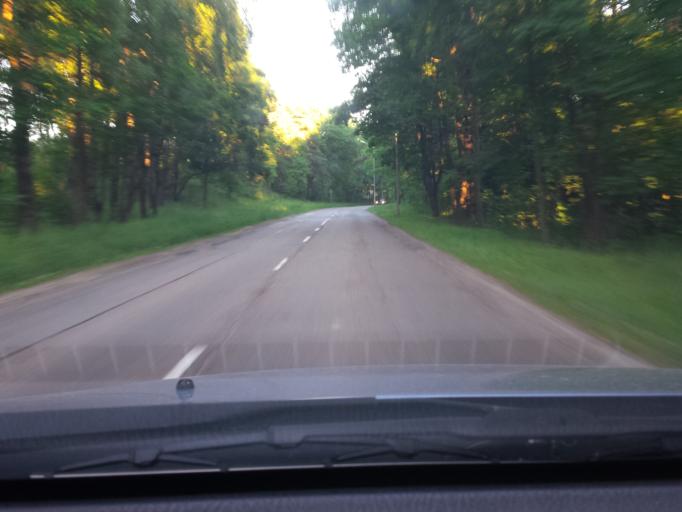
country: LV
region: Riga
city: Jaunciems
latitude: 57.0178
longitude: 24.2094
